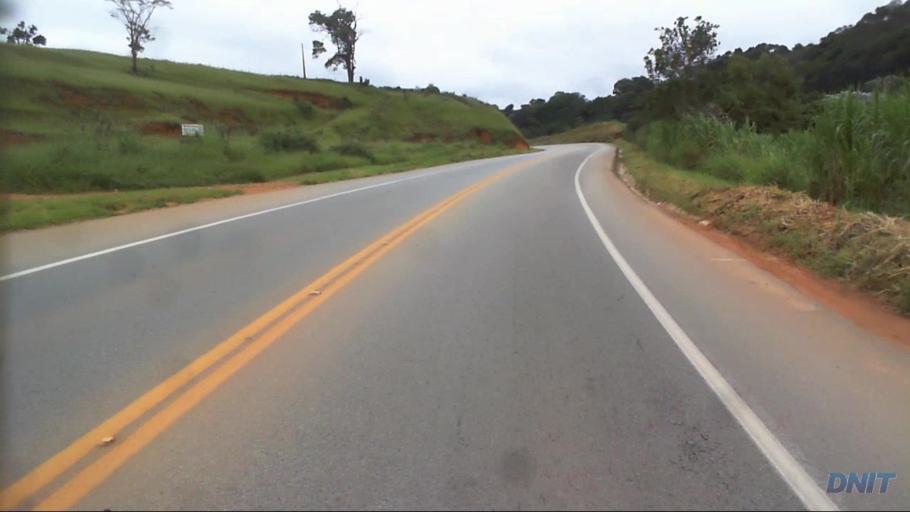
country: BR
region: Minas Gerais
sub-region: Joao Monlevade
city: Joao Monlevade
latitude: -19.8496
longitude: -43.2084
